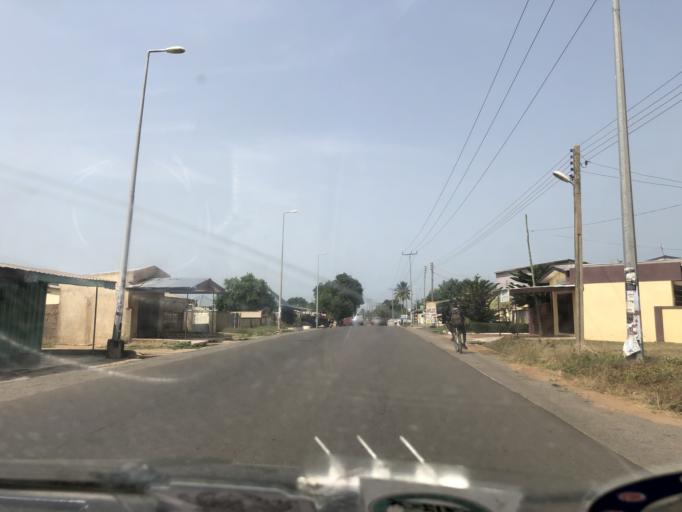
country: GH
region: Eastern
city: Koforidua
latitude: 6.0913
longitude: -0.2715
